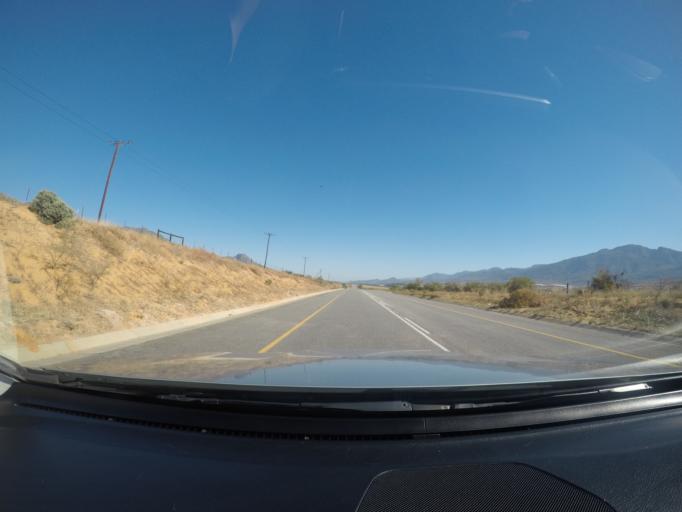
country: ZA
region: Western Cape
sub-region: West Coast District Municipality
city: Piketberg
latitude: -32.5923
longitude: 18.9894
